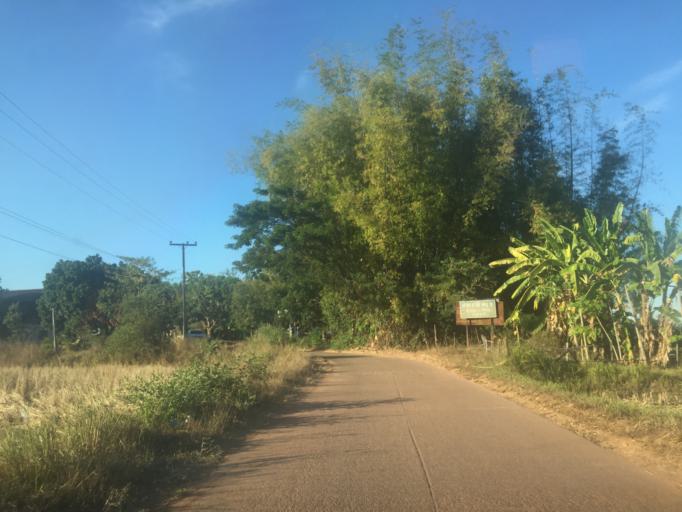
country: TH
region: Kalasin
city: Tha Khantho
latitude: 16.9829
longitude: 103.2640
